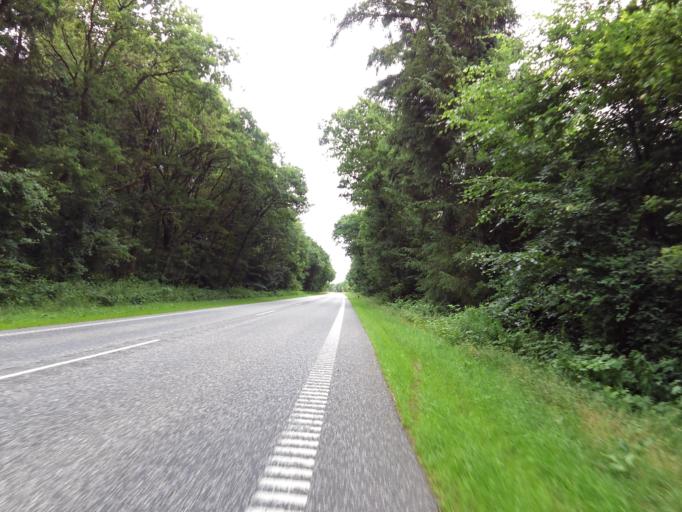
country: DK
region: South Denmark
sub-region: Tonder Kommune
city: Logumkloster
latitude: 55.0969
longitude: 8.9394
